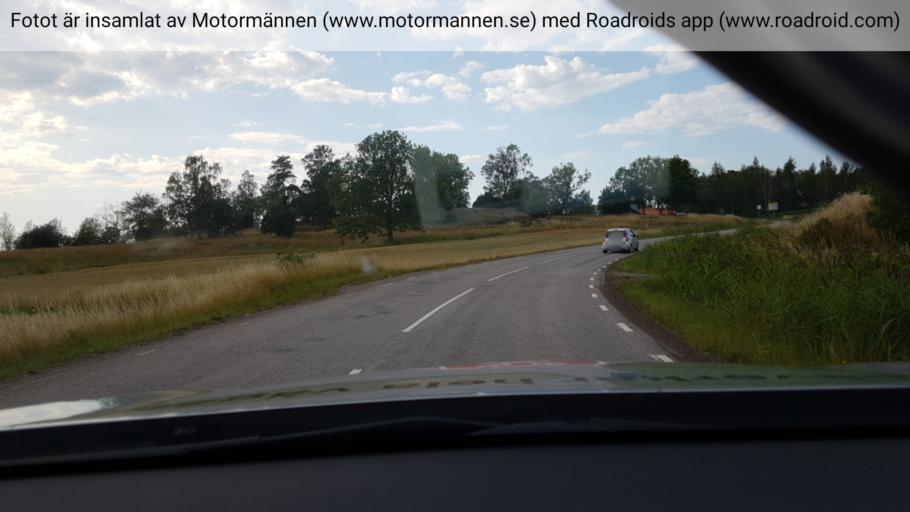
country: SE
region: Vaestra Goetaland
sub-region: Lidkopings Kommun
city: Lidkoping
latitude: 58.5852
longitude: 13.1197
